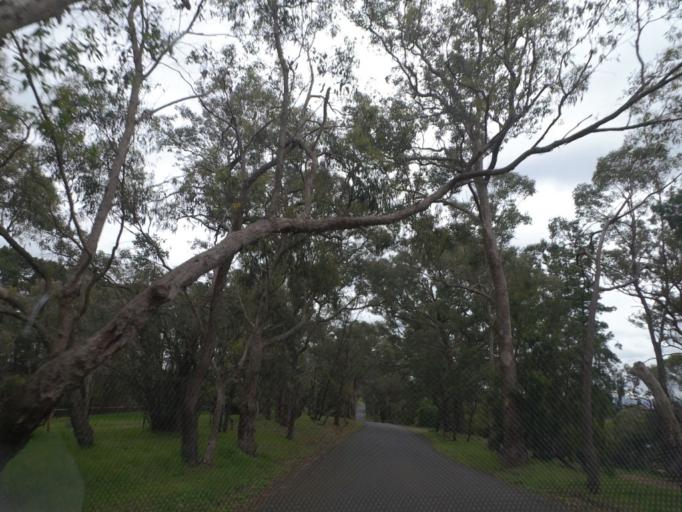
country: AU
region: Victoria
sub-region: Nillumbik
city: Hurstbridge
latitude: -37.6609
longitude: 145.2154
